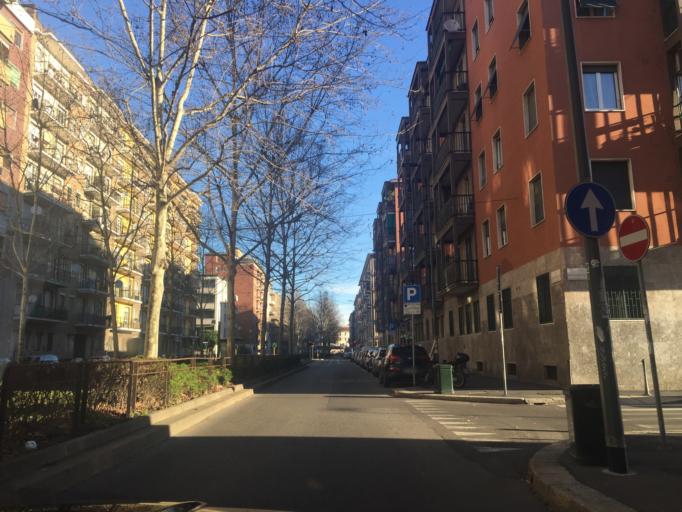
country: IT
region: Lombardy
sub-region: Citta metropolitana di Milano
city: Milano
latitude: 45.4399
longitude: 9.1833
